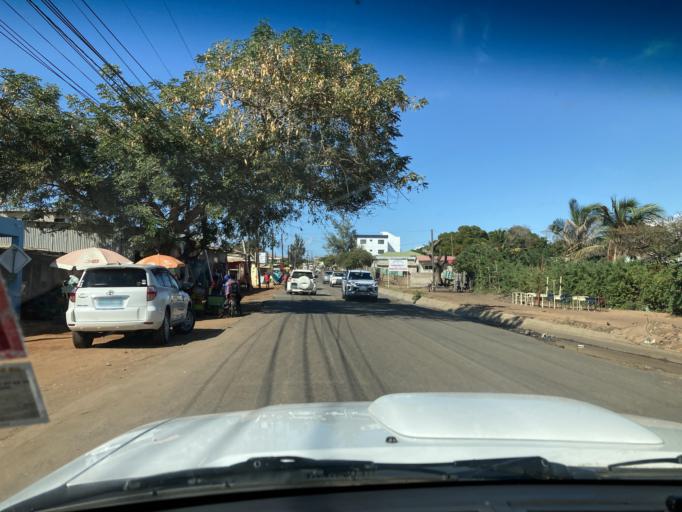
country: MZ
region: Cabo Delgado
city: Pemba
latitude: -12.9795
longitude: 40.5414
